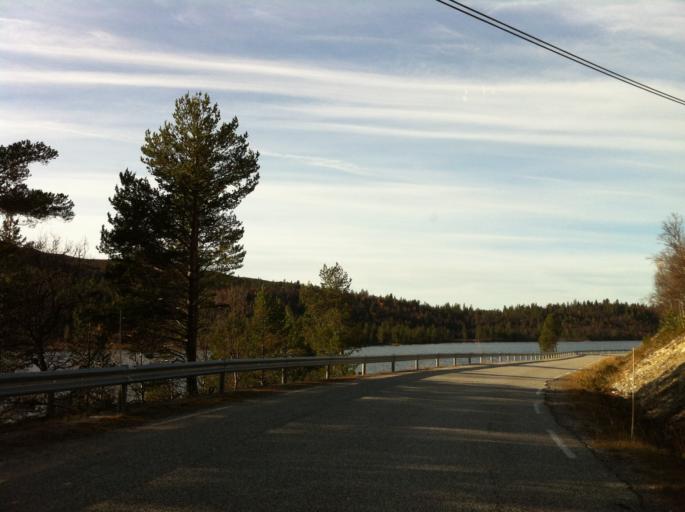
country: NO
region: Hedmark
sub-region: Engerdal
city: Engerdal
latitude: 62.0966
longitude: 12.0334
